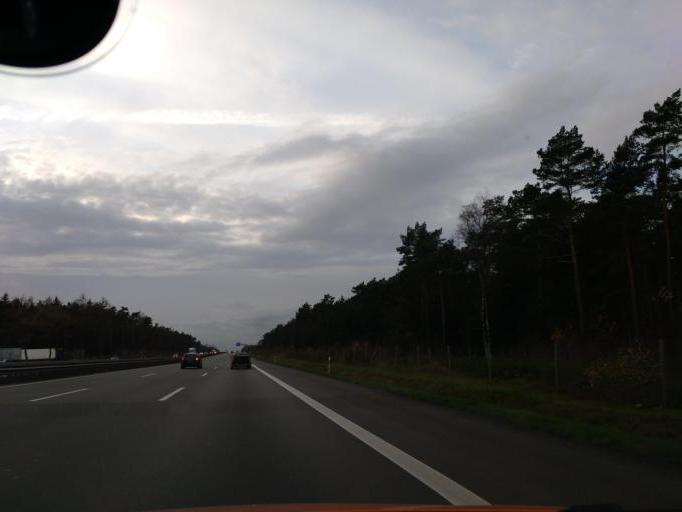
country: DE
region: Lower Saxony
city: Heidenau
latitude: 53.3438
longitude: 9.6566
